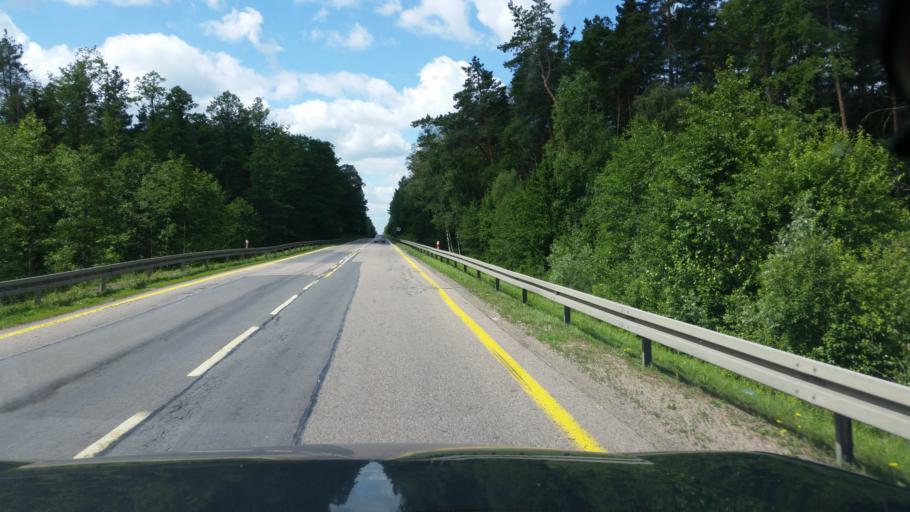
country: PL
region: Podlasie
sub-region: Powiat grajewski
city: Rajgrod
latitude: 53.6983
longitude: 22.6509
